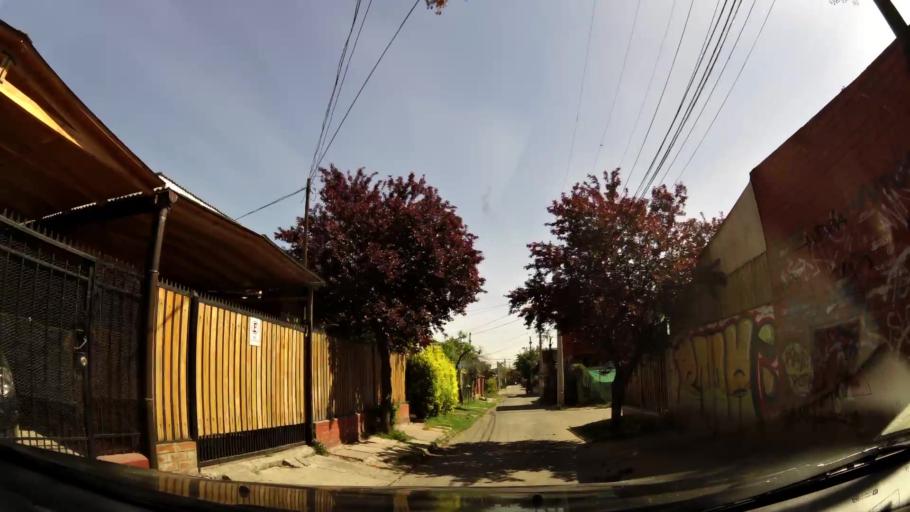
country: CL
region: Santiago Metropolitan
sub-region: Provincia de Cordillera
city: Puente Alto
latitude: -33.5700
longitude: -70.5678
